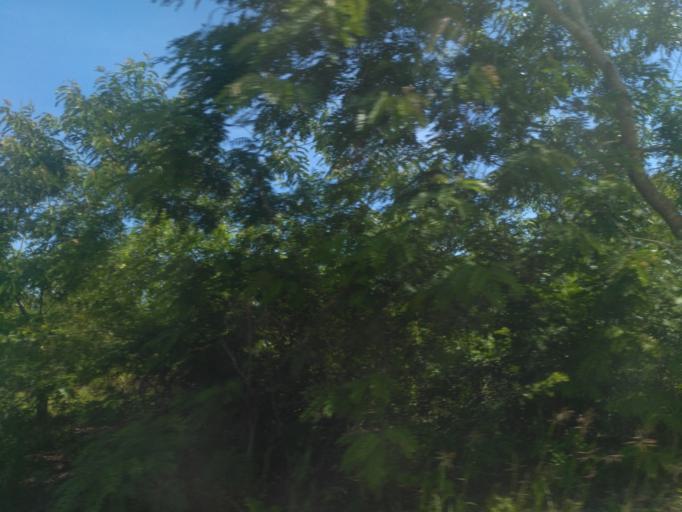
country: TZ
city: Kiwengwa
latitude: -5.9877
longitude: 39.3342
